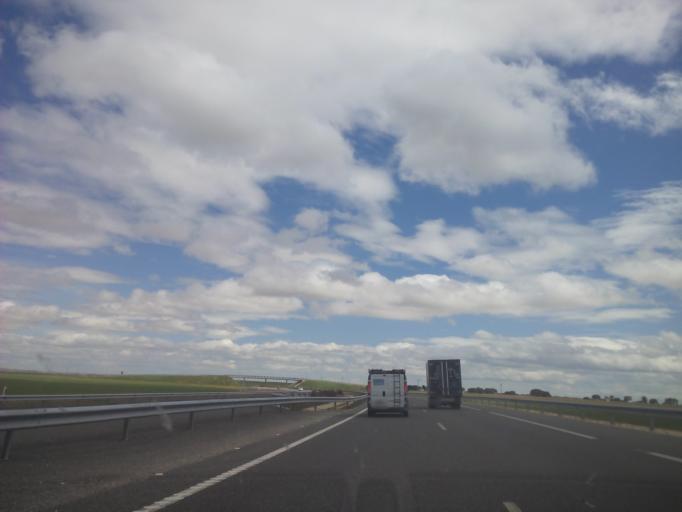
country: ES
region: Castille and Leon
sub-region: Provincia de Salamanca
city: Pelabravo
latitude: 40.9288
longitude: -5.5814
